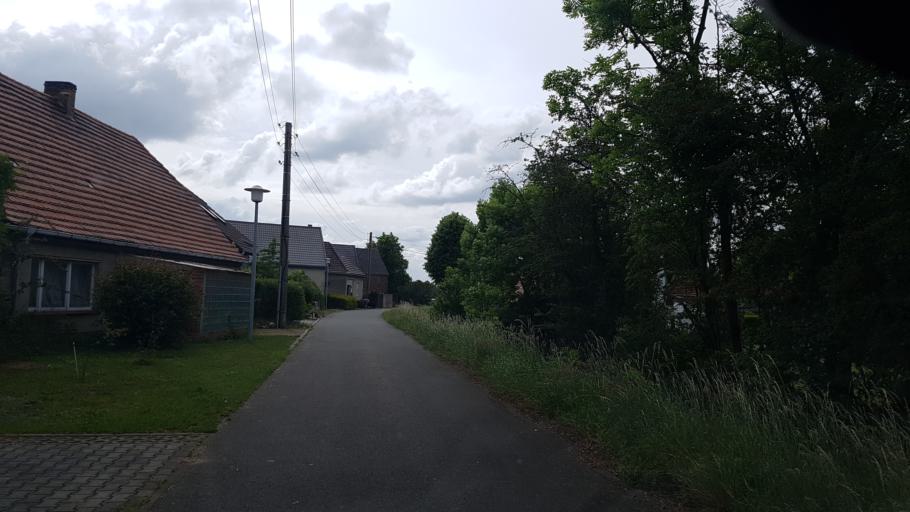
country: DE
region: Brandenburg
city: Luckau
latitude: 51.8280
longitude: 13.7590
